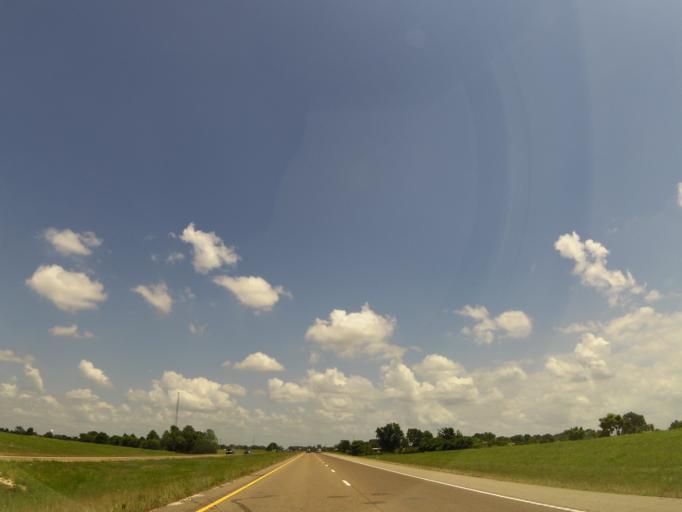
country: US
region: Tennessee
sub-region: Crockett County
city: Alamo
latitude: 35.7855
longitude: -89.1480
